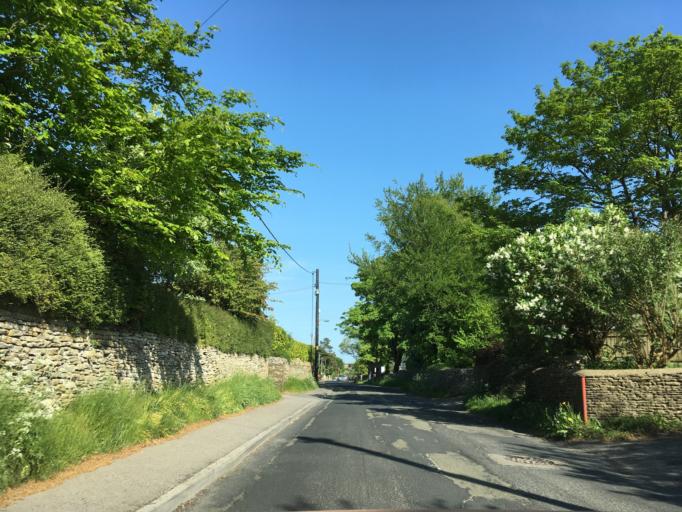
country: GB
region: England
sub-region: Gloucestershire
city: Minchinhampton
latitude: 51.7067
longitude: -2.1990
